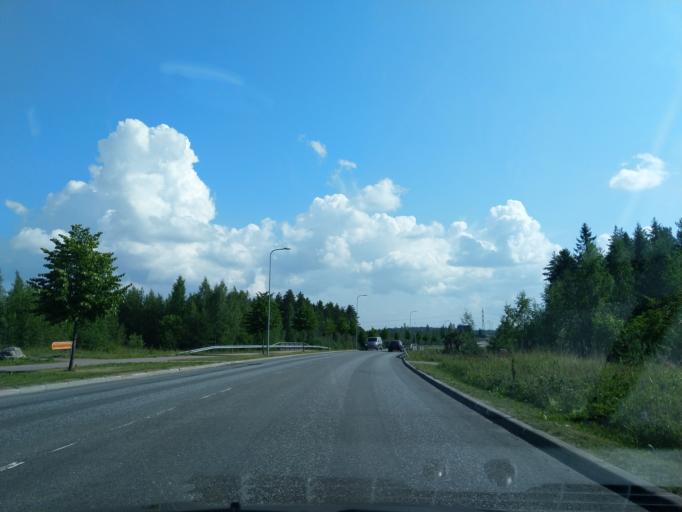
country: FI
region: South Karelia
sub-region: Lappeenranta
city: Lappeenranta
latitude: 61.0383
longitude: 28.1142
